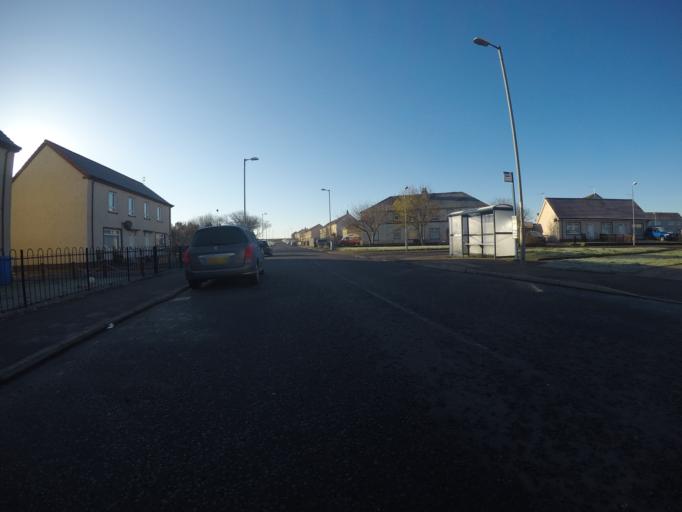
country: GB
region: Scotland
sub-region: North Ayrshire
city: Stevenston
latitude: 55.6325
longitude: -4.7425
